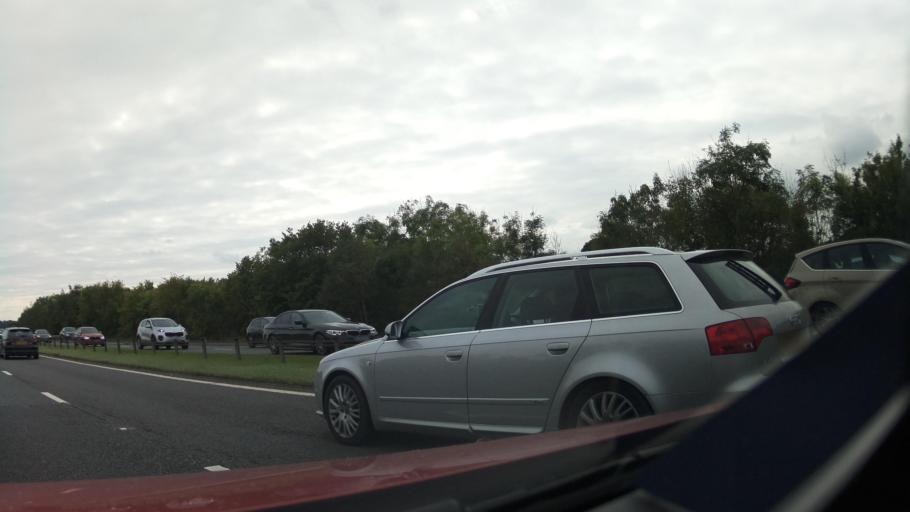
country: GB
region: England
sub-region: County Durham
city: West Rainton
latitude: 54.8066
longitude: -1.5227
